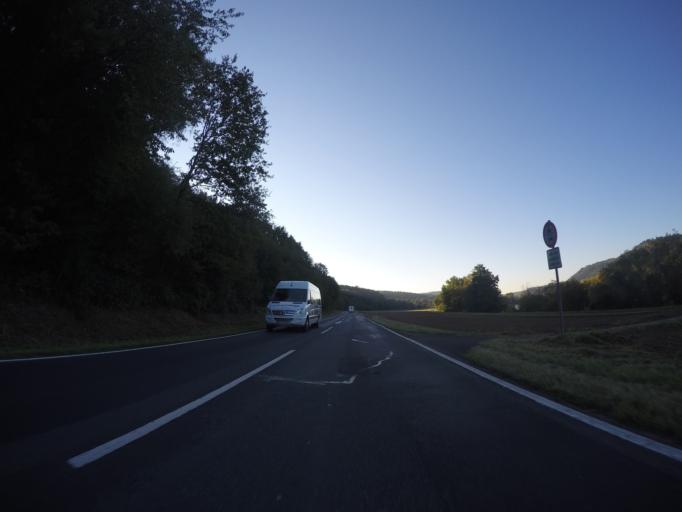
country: DE
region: Bavaria
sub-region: Regierungsbezirk Unterfranken
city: Kreuzwertheim
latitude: 49.7843
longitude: 9.5122
